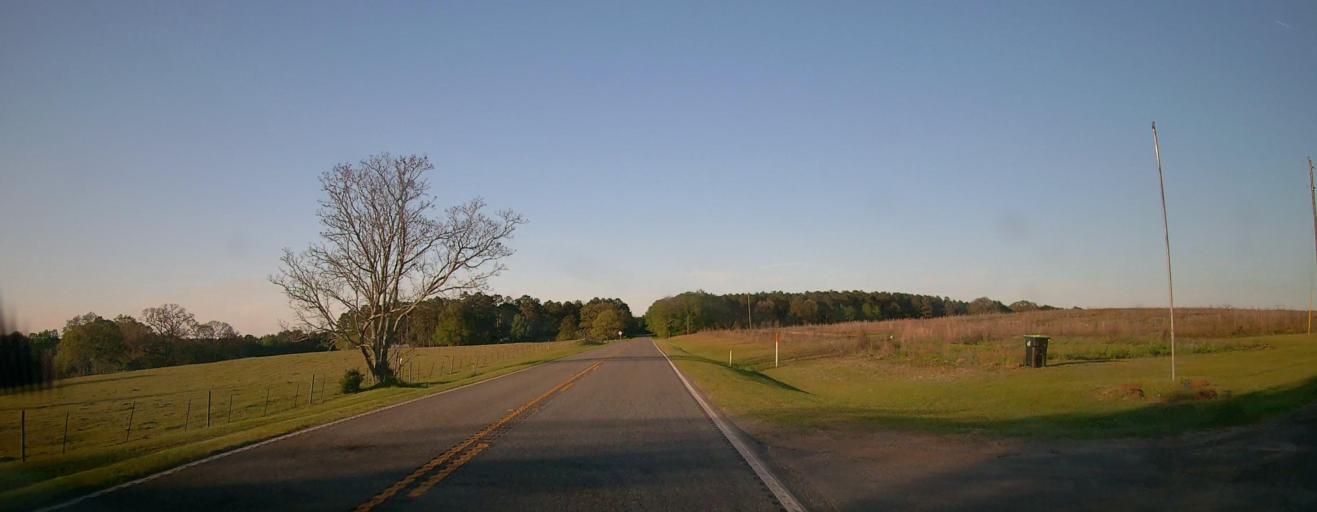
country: US
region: Georgia
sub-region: Marion County
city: Buena Vista
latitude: 32.3999
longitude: -84.4424
